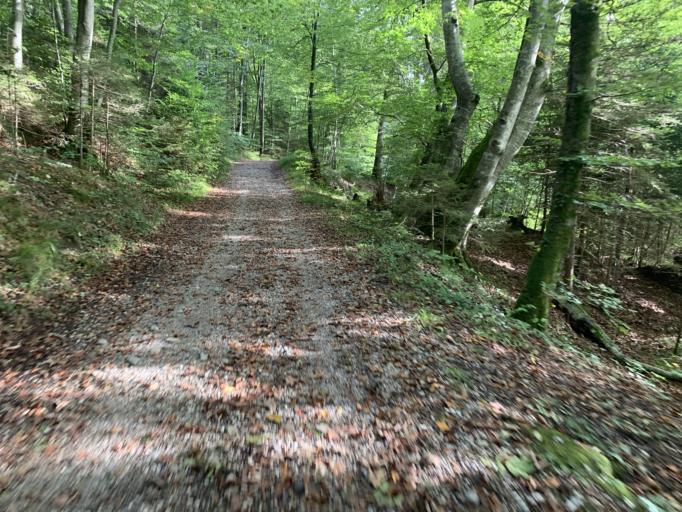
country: DE
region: Bavaria
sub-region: Upper Bavaria
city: Baierbrunn
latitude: 48.0214
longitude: 11.4983
